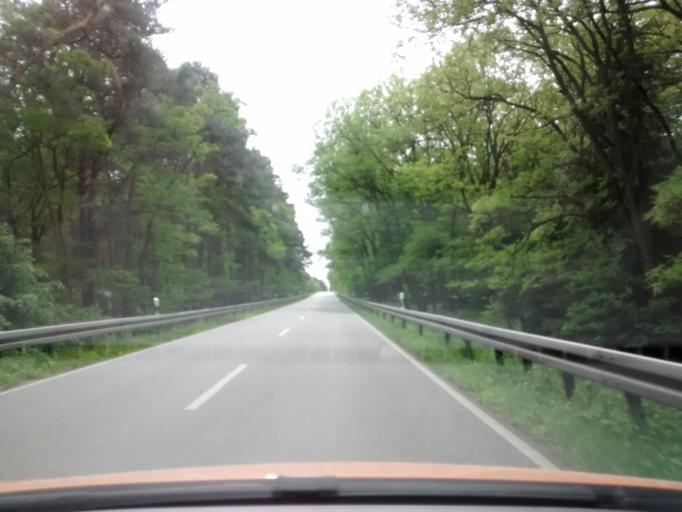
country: DE
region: Saxony-Anhalt
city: Holzdorf
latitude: 51.8843
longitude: 13.1425
